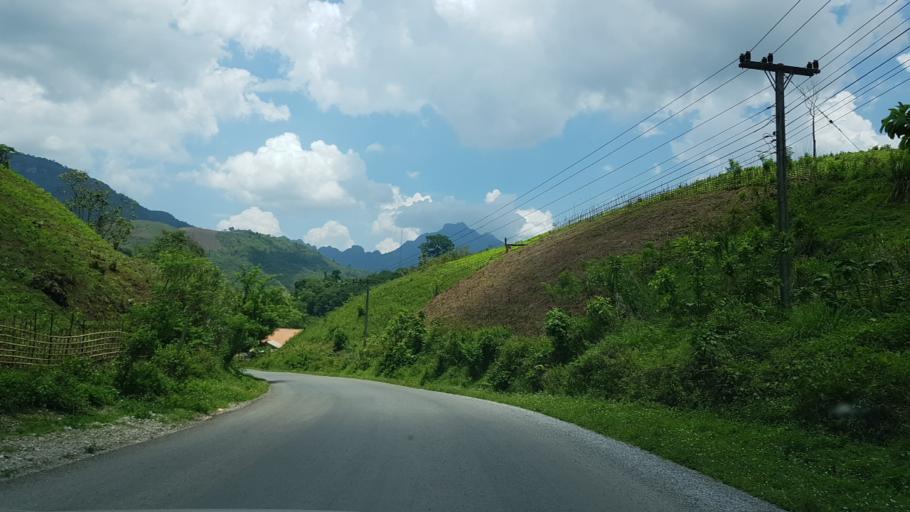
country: LA
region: Vientiane
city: Muang Kasi
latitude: 19.1389
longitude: 102.3071
